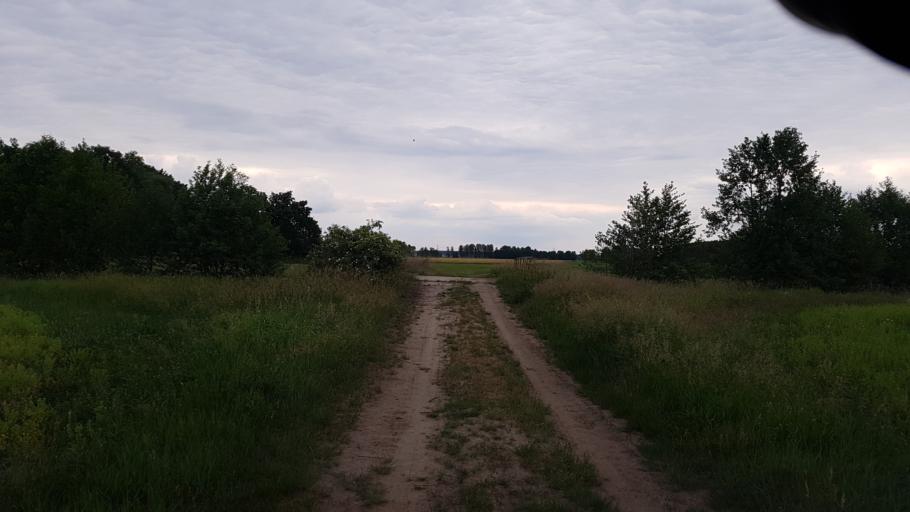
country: DE
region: Brandenburg
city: Ihlow
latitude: 51.8152
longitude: 13.2387
